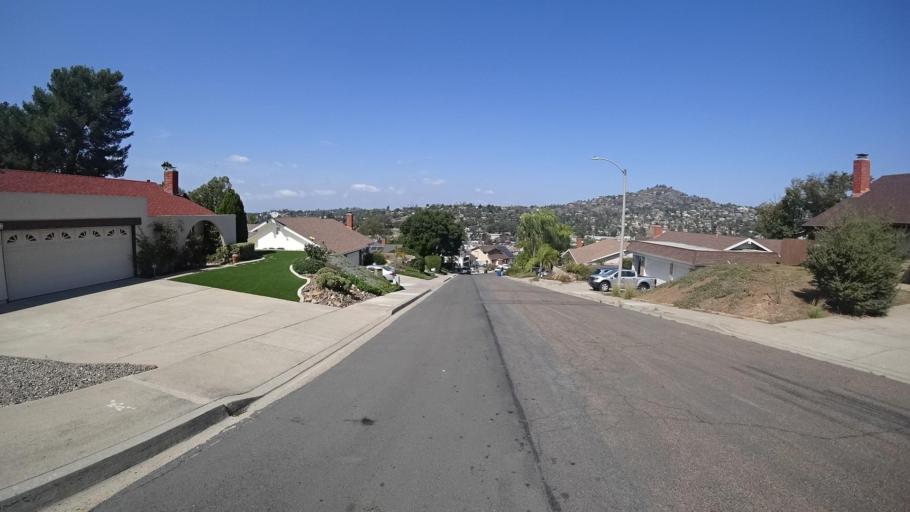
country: US
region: California
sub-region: San Diego County
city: Spring Valley
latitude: 32.7429
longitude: -116.9854
